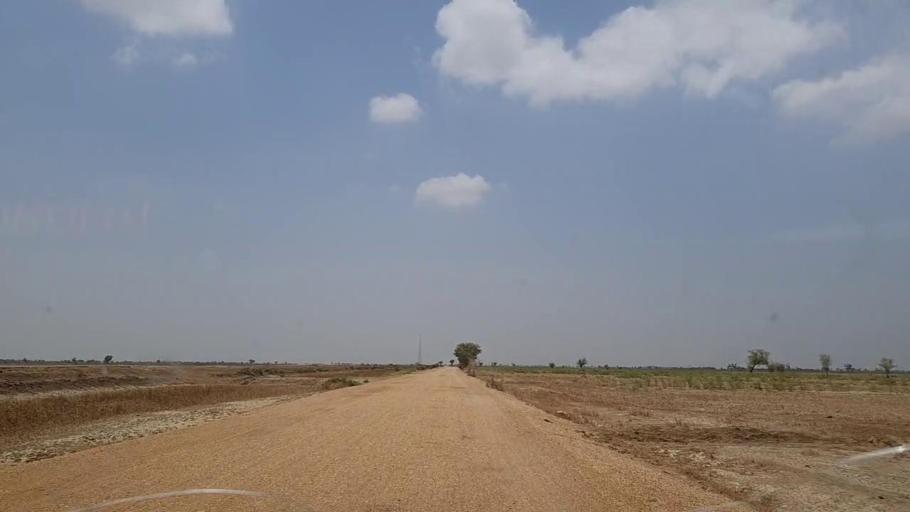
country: PK
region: Sindh
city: Johi
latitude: 26.7745
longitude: 67.6544
